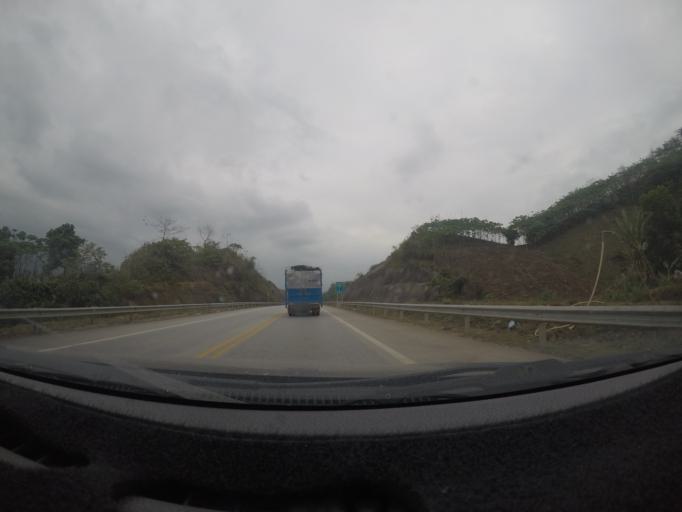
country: VN
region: Lao Cai
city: Thi Tran Pho Rang
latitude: 22.1069
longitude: 104.4099
